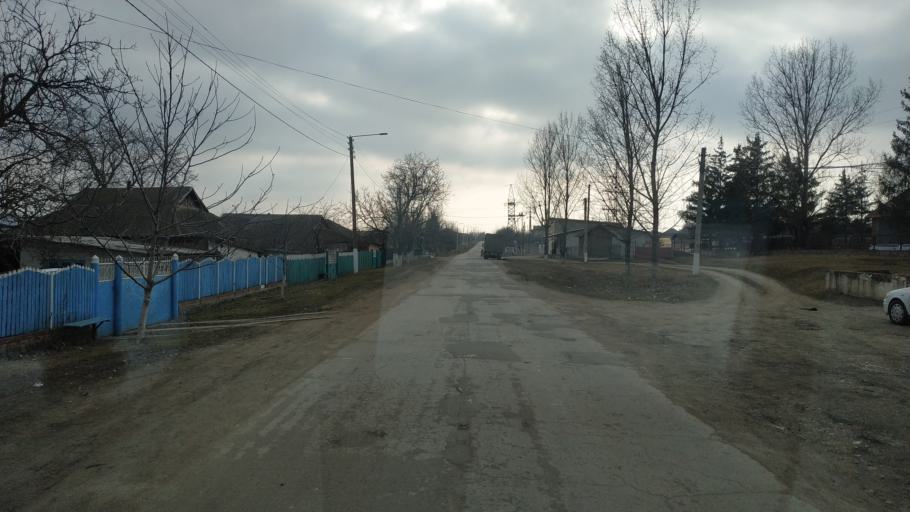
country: MD
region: Hincesti
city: Dancu
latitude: 46.8211
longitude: 28.2749
